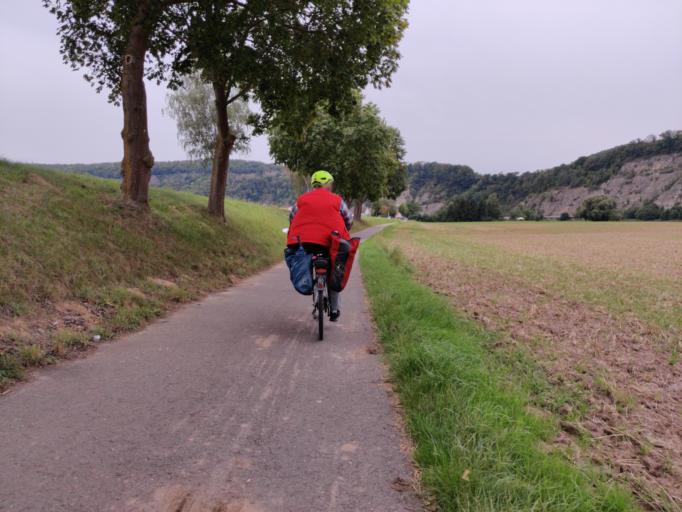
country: DE
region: Lower Saxony
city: Pegestorf
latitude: 51.9263
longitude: 9.4733
